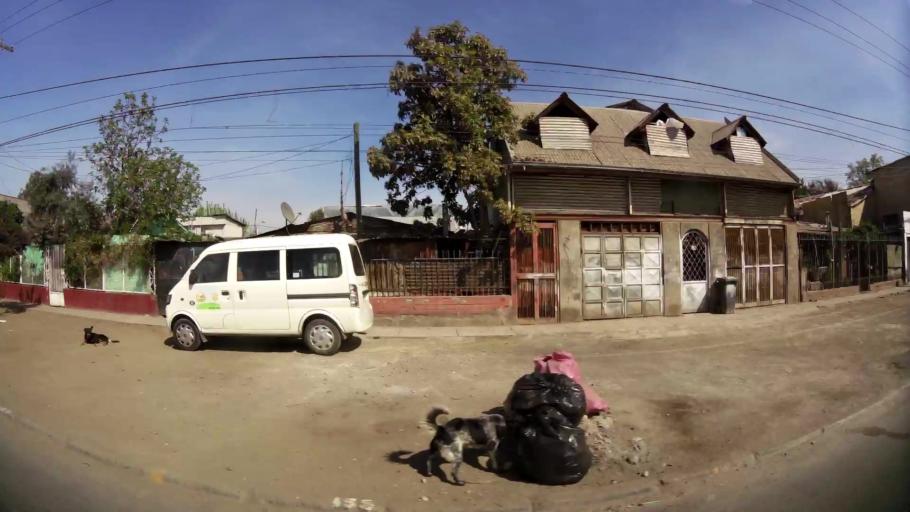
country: CL
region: Santiago Metropolitan
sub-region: Provincia de Santiago
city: Lo Prado
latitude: -33.4206
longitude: -70.7476
